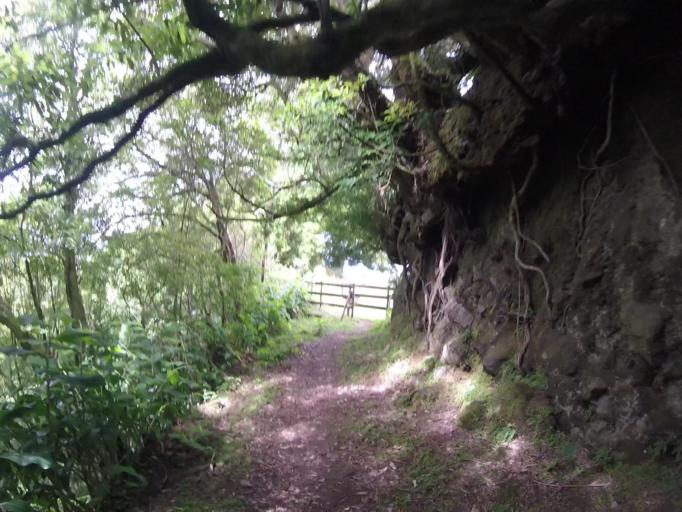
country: PT
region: Azores
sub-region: Vila Franca do Campo
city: Vila Franca do Campo
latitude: 37.7466
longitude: -25.5105
